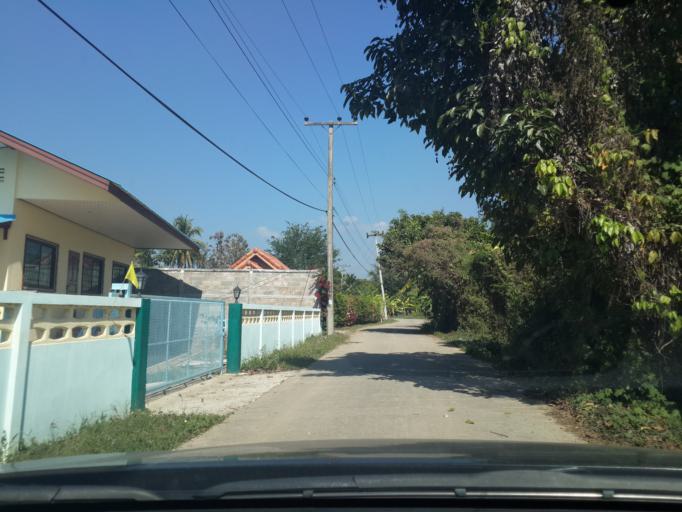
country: TH
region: Chiang Mai
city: San Sai
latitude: 18.8861
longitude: 99.1154
